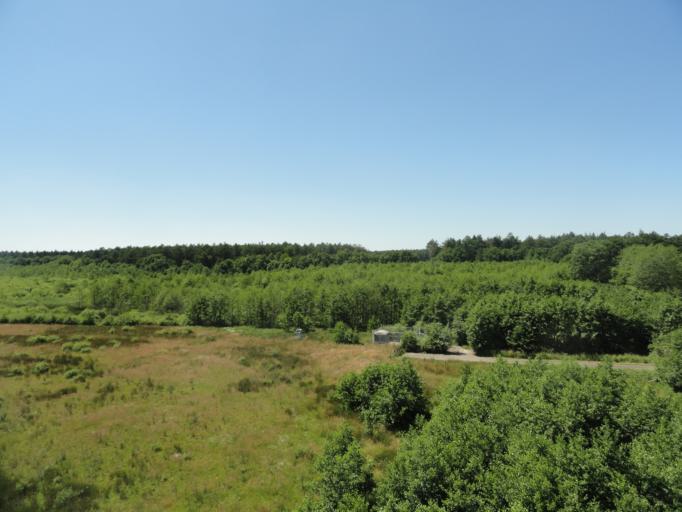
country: NL
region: Drenthe
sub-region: Gemeente Assen
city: Assen
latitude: 52.9124
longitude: 6.6295
